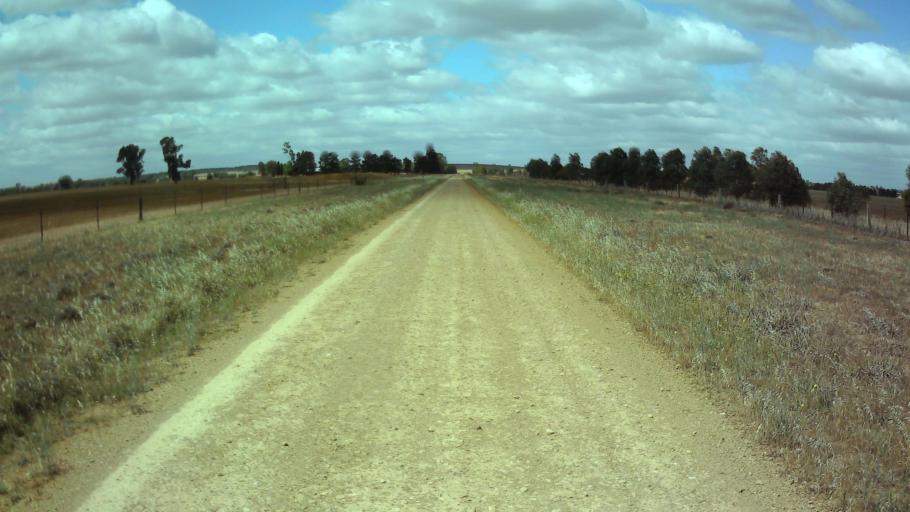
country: AU
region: New South Wales
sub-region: Weddin
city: Grenfell
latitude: -34.0551
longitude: 148.3313
